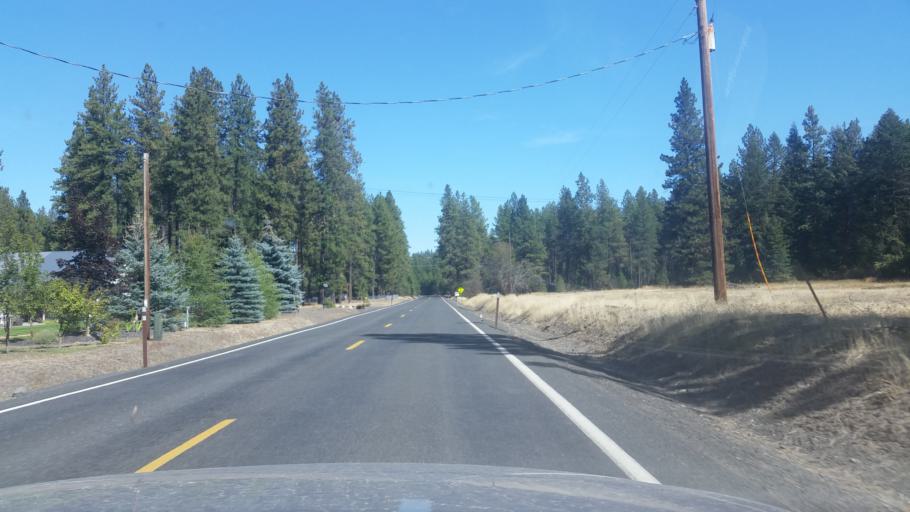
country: US
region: Washington
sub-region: Spokane County
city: Spokane
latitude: 47.5704
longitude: -117.4796
